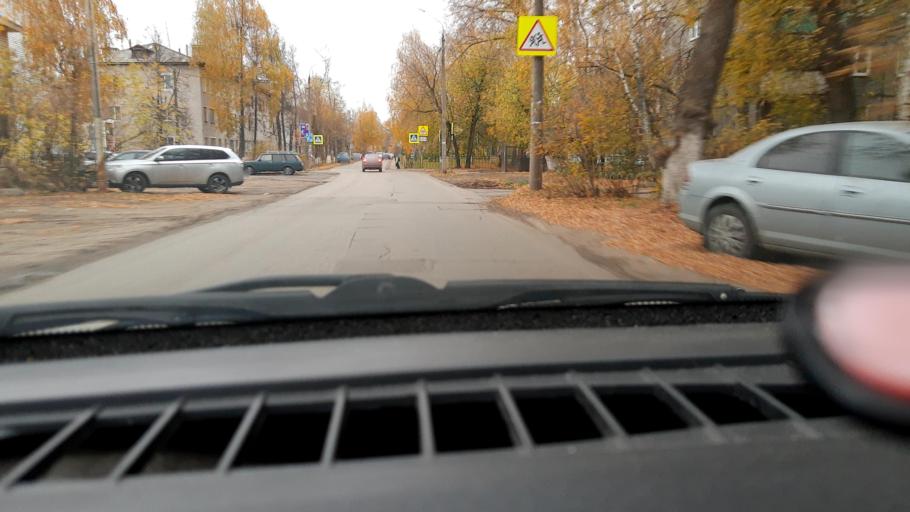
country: RU
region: Nizjnij Novgorod
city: Gorbatovka
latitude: 56.3526
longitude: 43.8375
